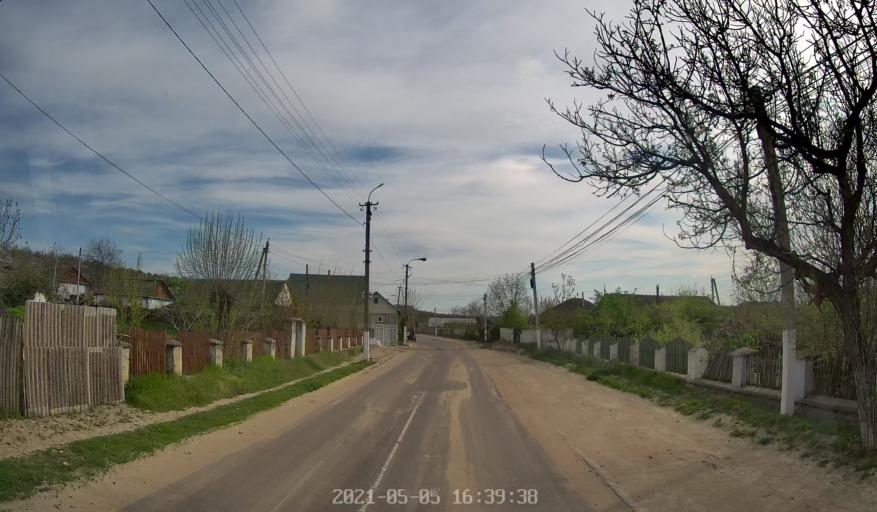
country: MD
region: Criuleni
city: Criuleni
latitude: 47.1254
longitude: 29.1938
